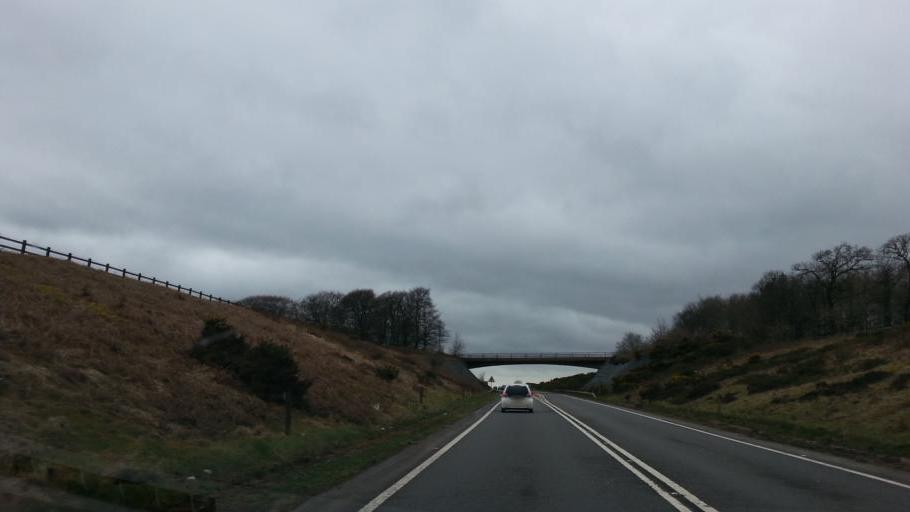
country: GB
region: England
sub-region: Devon
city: Tiverton
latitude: 50.9773
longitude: -3.6354
